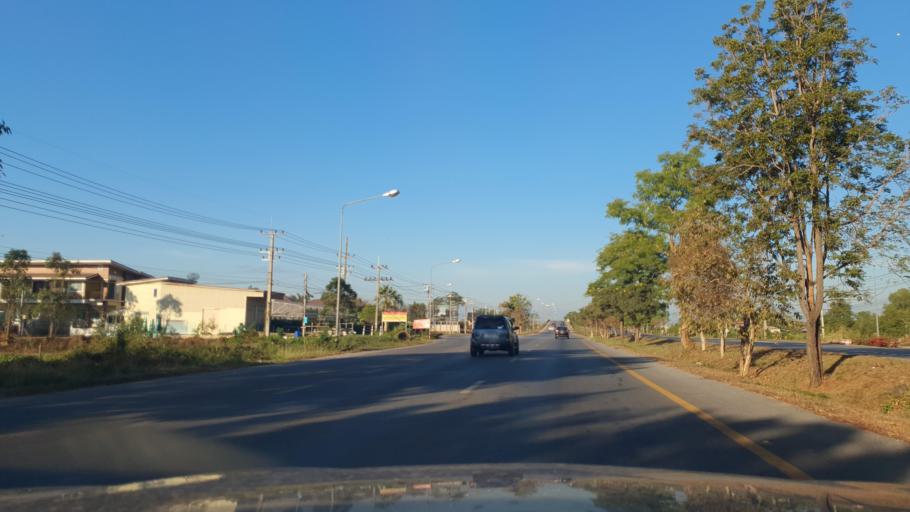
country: TH
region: Phitsanulok
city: Phitsanulok
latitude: 16.8644
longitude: 100.2714
